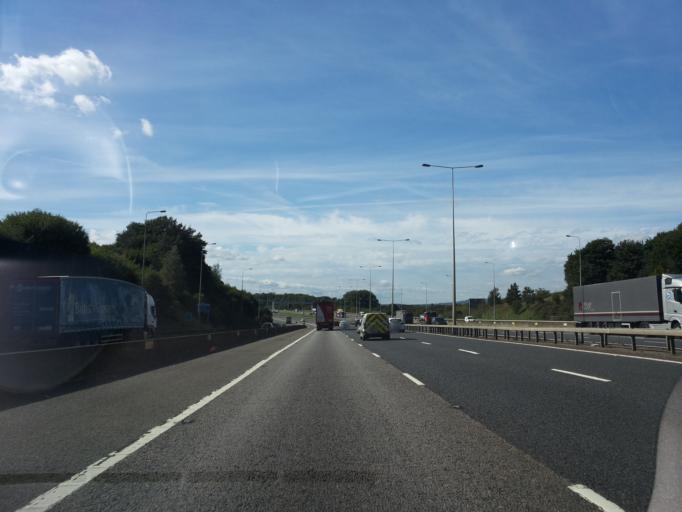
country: GB
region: England
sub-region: Kent
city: Aylesford
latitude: 51.2983
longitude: 0.5067
